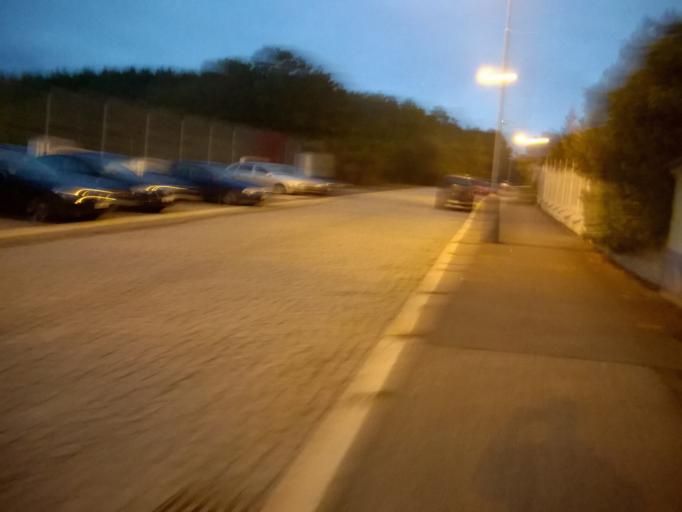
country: CZ
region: Praha
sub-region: Praha 9
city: Vysocany
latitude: 50.0994
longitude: 14.5056
